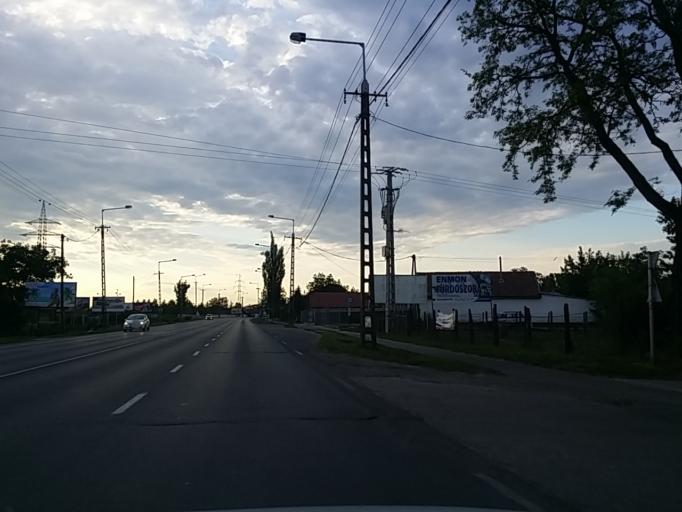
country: HU
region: Bacs-Kiskun
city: Kecskemet
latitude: 46.9260
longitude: 19.6690
